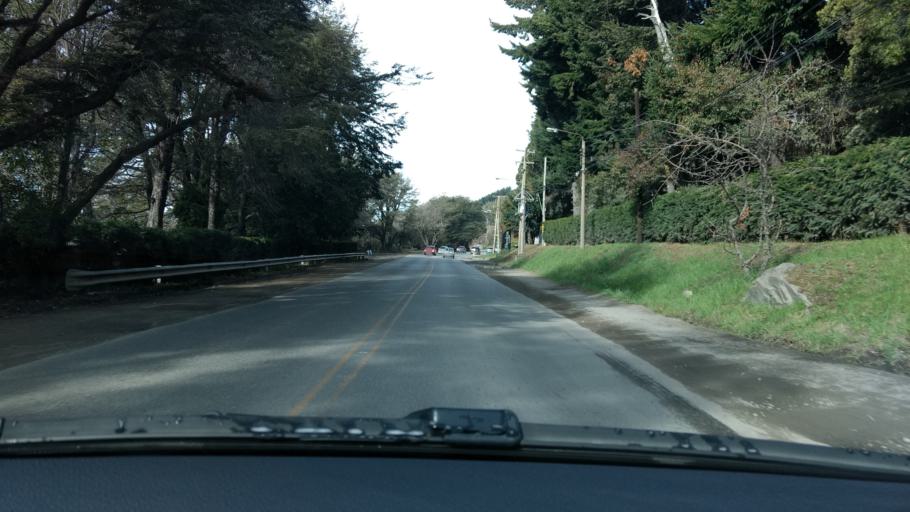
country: AR
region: Rio Negro
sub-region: Departamento de Bariloche
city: San Carlos de Bariloche
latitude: -41.1314
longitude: -71.3394
